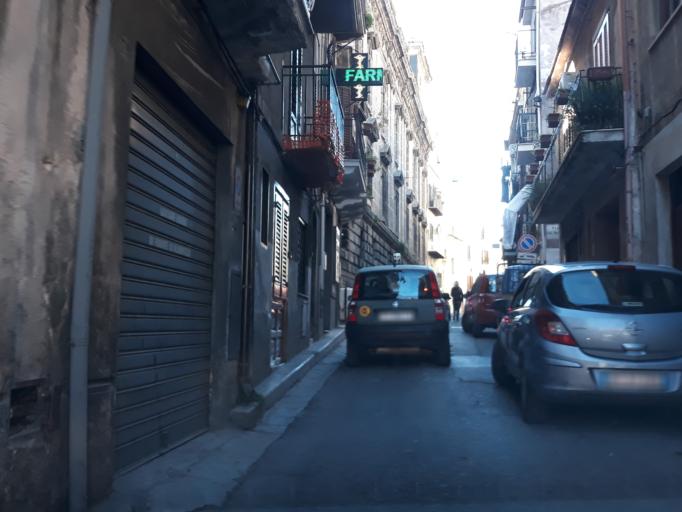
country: IT
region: Sicily
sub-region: Palermo
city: Monreale
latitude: 38.0822
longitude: 13.2903
